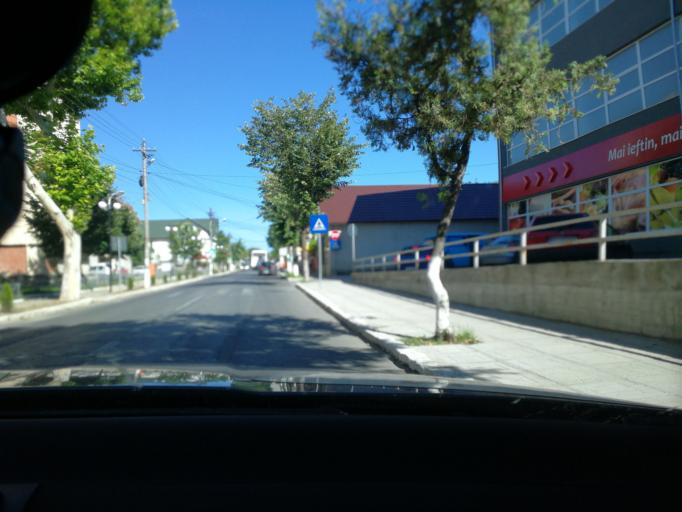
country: RO
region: Tulcea
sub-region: Oras Macin
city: Macin
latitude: 45.2442
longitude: 28.1330
